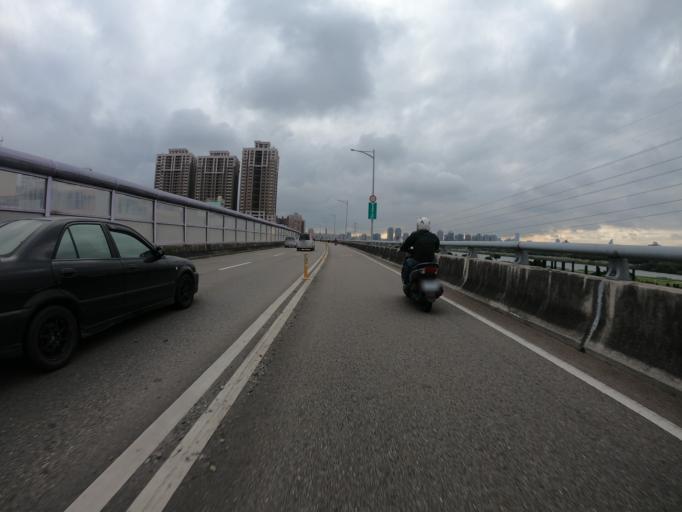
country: TW
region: Taipei
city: Taipei
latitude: 25.0189
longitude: 121.5098
